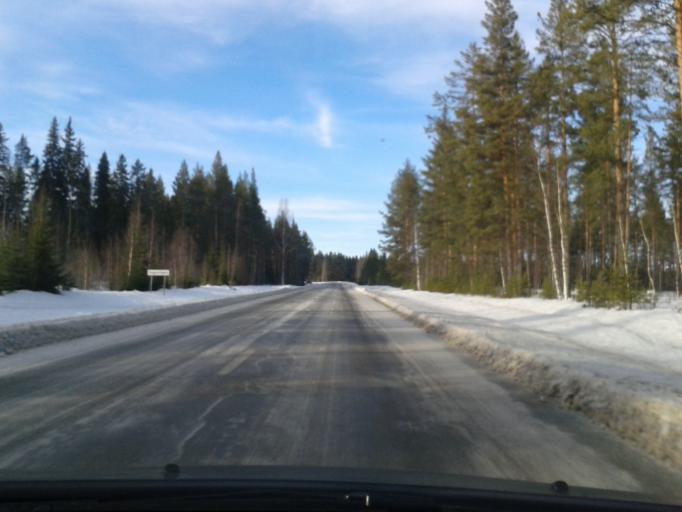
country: SE
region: Vaesternorrland
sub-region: OErnskoeldsviks Kommun
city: Bredbyn
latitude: 63.5403
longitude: 17.9600
